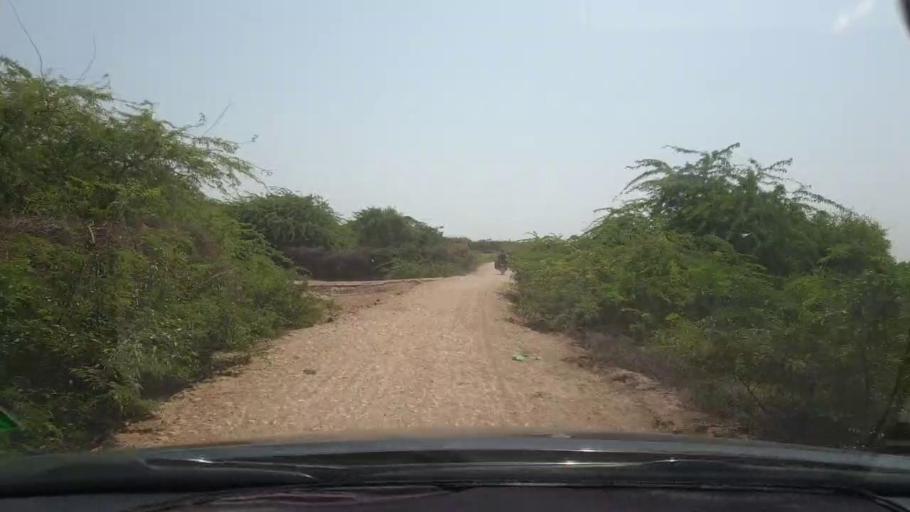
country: PK
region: Sindh
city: Tando Bago
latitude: 24.8031
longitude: 69.1833
